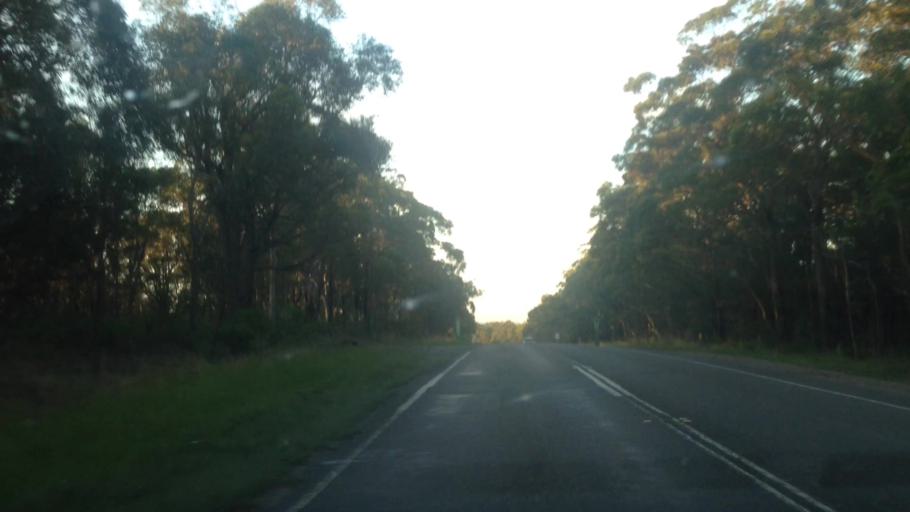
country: AU
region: New South Wales
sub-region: Lake Macquarie Shire
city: Dora Creek
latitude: -33.1506
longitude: 151.4792
